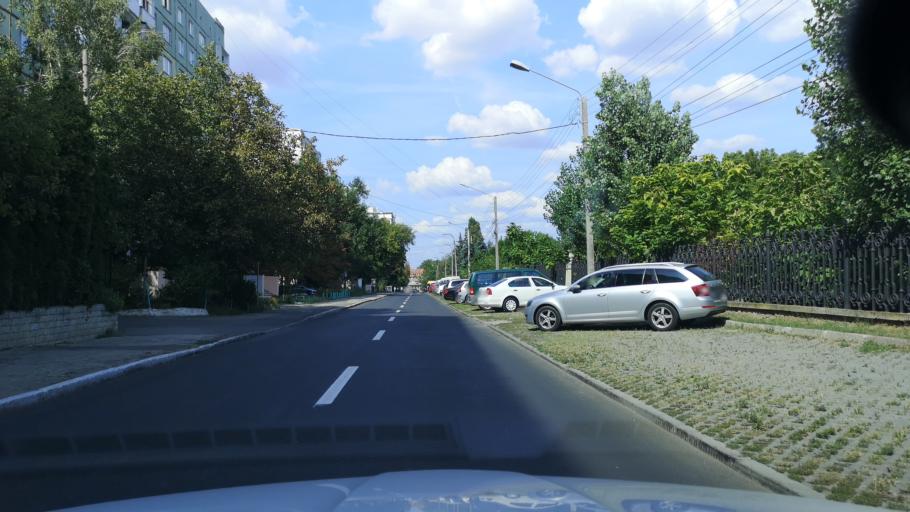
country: MD
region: Chisinau
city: Chisinau
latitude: 47.0292
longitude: 28.8080
